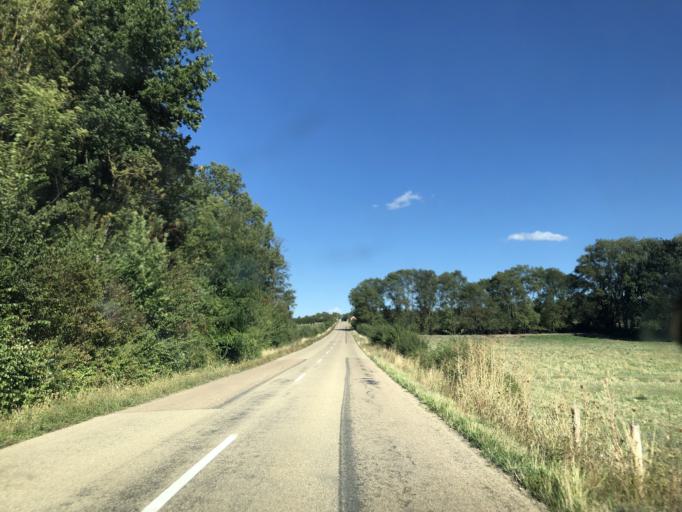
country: FR
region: Bourgogne
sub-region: Departement de l'Yonne
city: Seignelay
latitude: 47.9003
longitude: 3.5830
